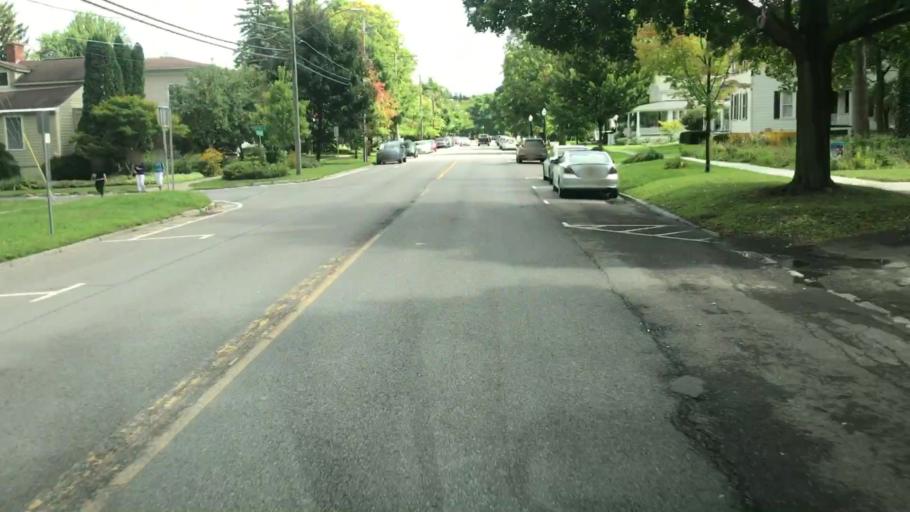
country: US
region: New York
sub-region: Onondaga County
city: Skaneateles
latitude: 42.9448
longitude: -76.4353
